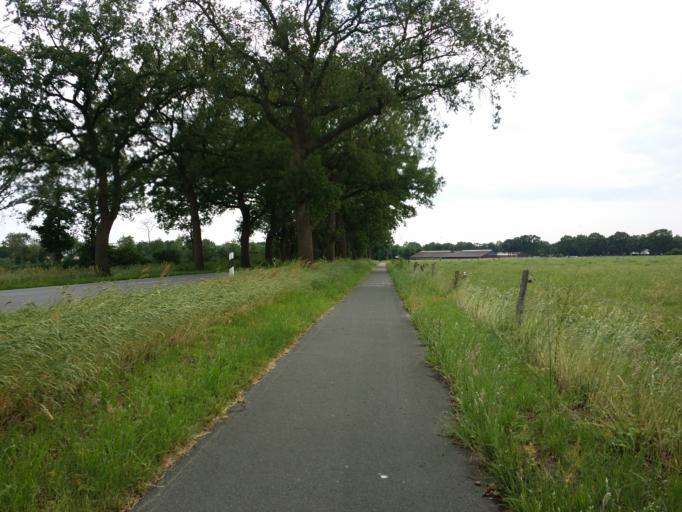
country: DE
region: Lower Saxony
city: Wiefelstede
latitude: 53.2695
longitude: 8.1111
